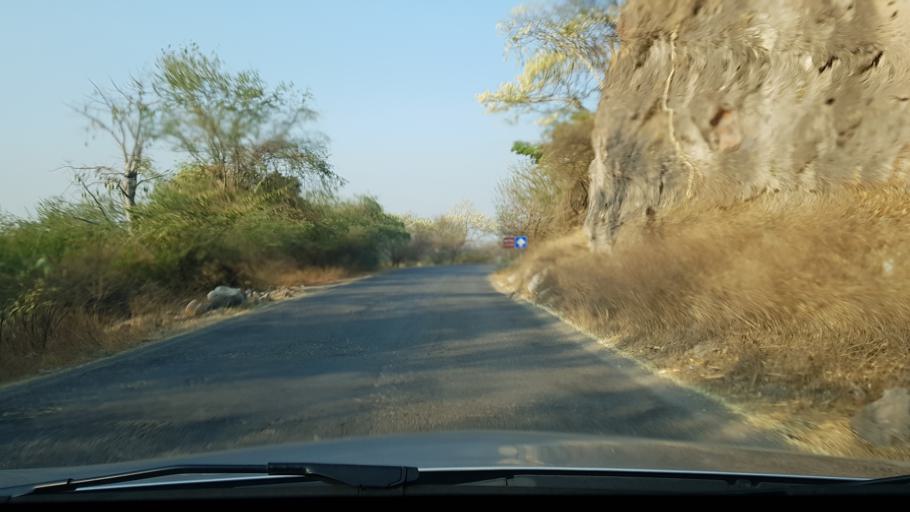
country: MX
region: Morelos
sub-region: Tepalcingo
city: Zacapalco
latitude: 18.6376
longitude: -99.0107
